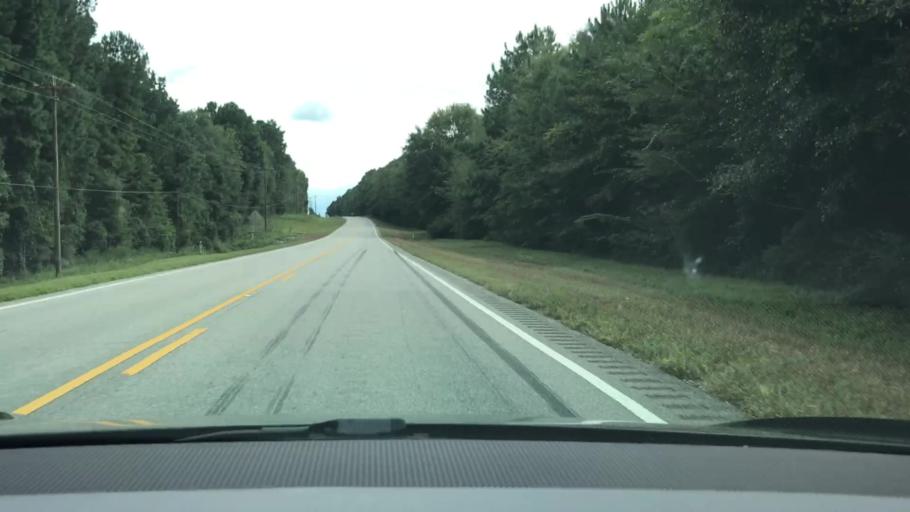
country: US
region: Alabama
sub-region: Pike County
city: Troy
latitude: 31.6439
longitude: -85.9707
